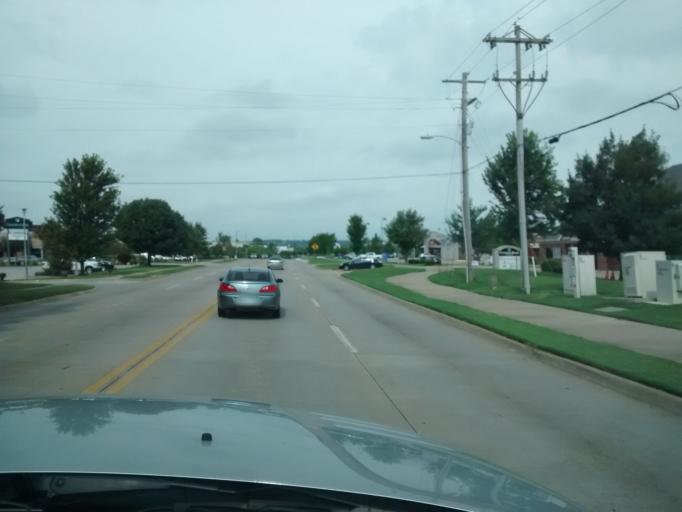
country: US
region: Arkansas
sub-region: Washington County
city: Johnson
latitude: 36.1202
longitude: -94.1352
